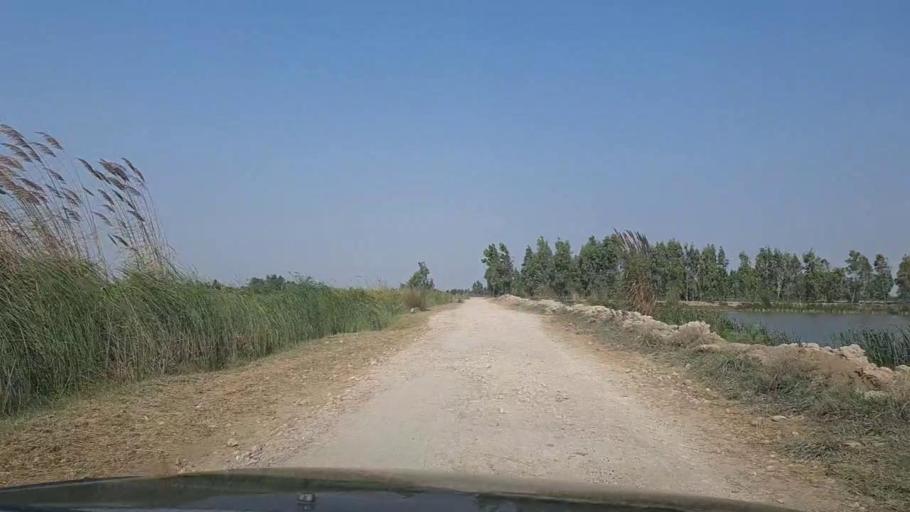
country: PK
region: Sindh
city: Thatta
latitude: 24.6213
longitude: 67.8150
